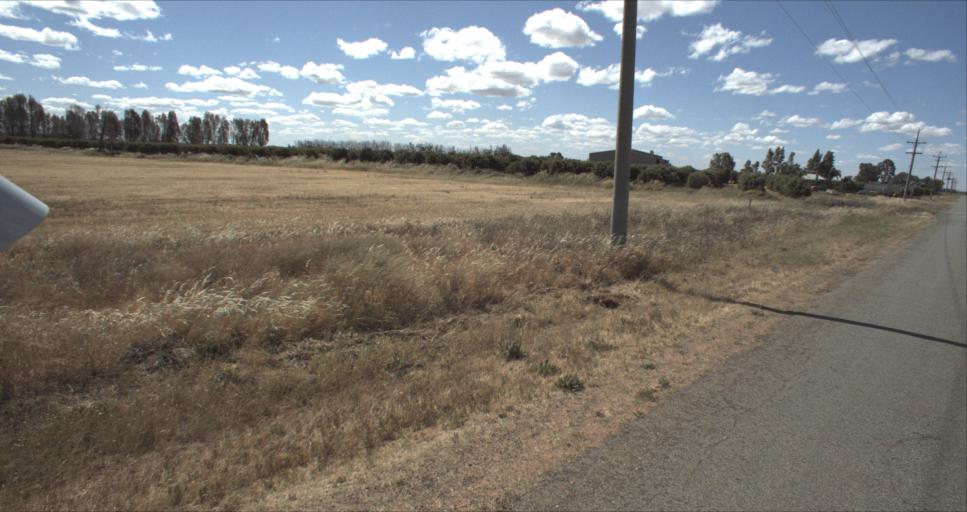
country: AU
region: New South Wales
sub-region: Leeton
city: Leeton
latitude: -34.5123
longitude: 146.2524
